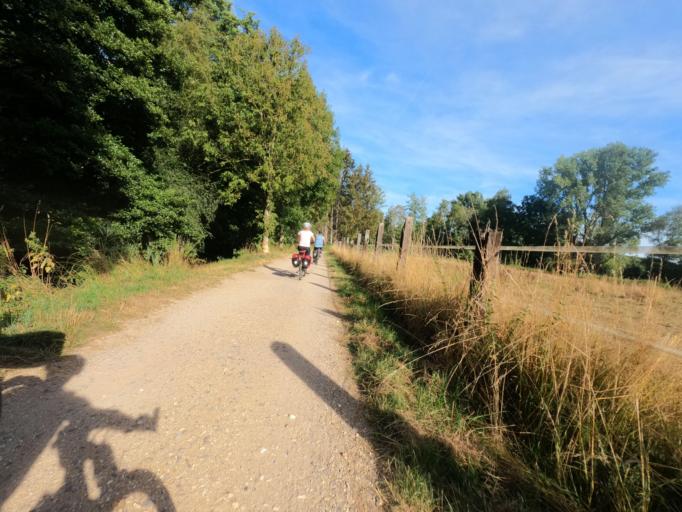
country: DE
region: North Rhine-Westphalia
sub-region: Regierungsbezirk Dusseldorf
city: Bruggen
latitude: 51.2362
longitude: 6.1416
